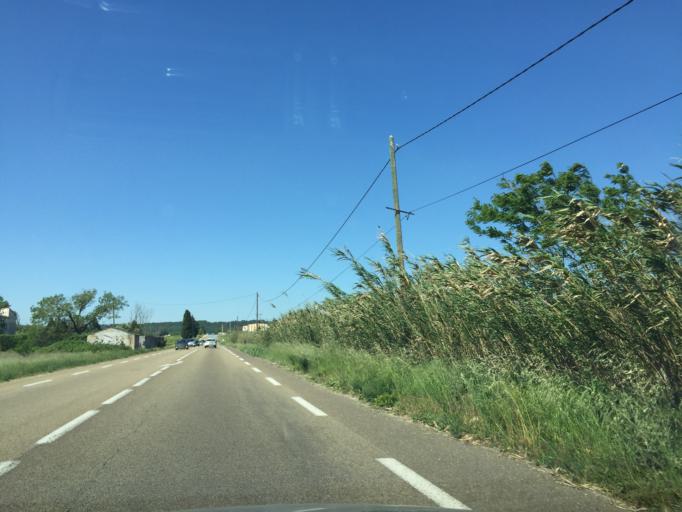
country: FR
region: Languedoc-Roussillon
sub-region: Departement du Gard
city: Saze
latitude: 43.9500
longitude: 4.7052
